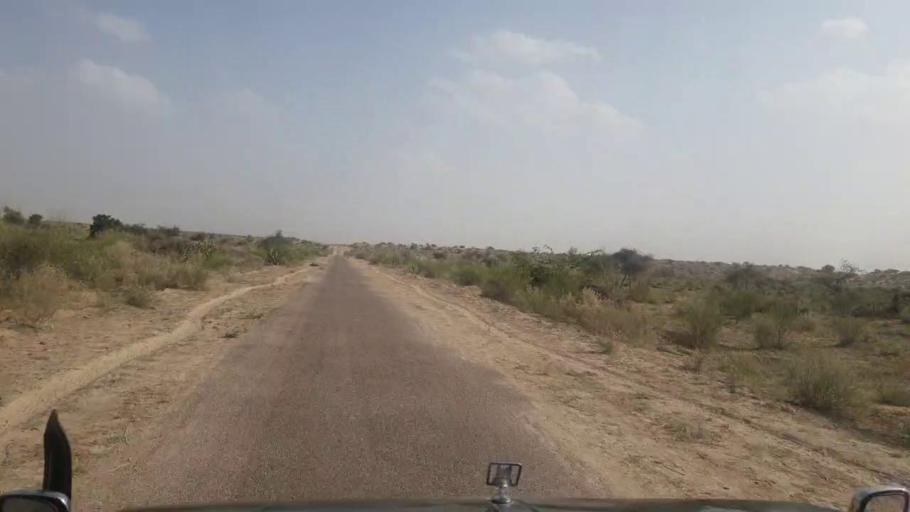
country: PK
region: Sindh
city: Islamkot
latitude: 25.1450
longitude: 70.3135
